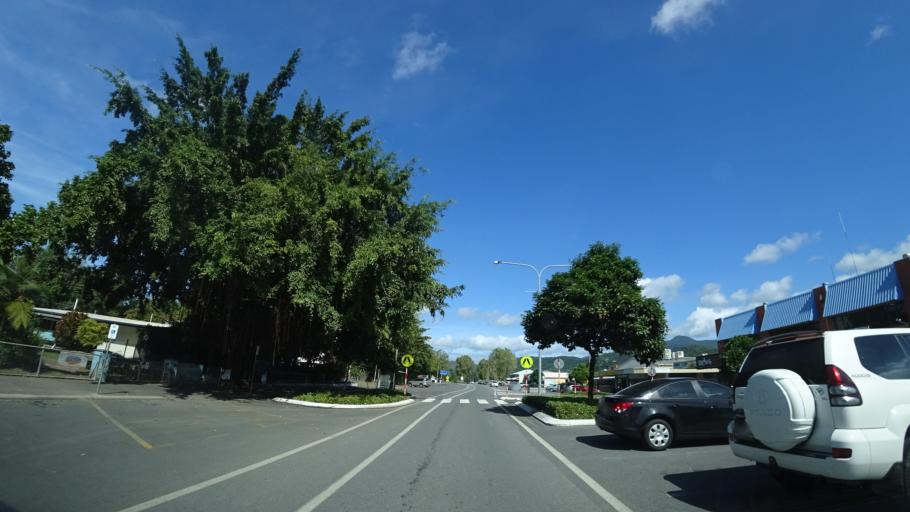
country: AU
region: Queensland
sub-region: Cairns
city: Port Douglas
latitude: -16.4617
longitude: 145.3736
